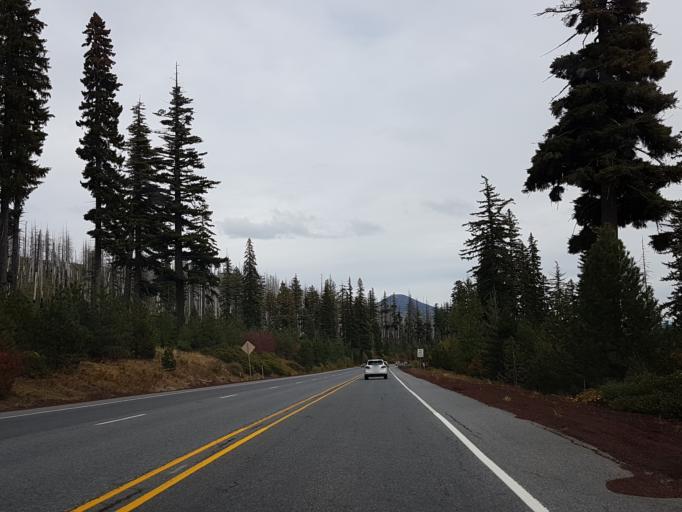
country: US
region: Oregon
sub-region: Deschutes County
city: Sisters
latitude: 44.4239
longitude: -121.7999
